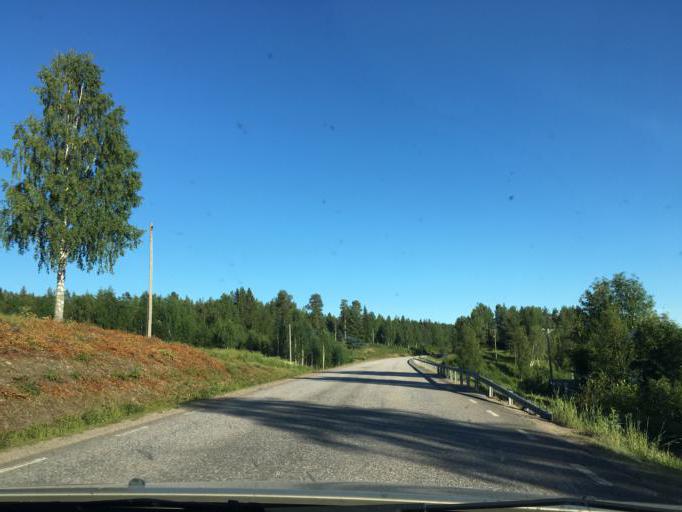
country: SE
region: Norrbotten
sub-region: Kalix Kommun
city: Rolfs
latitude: 65.9166
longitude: 22.9205
